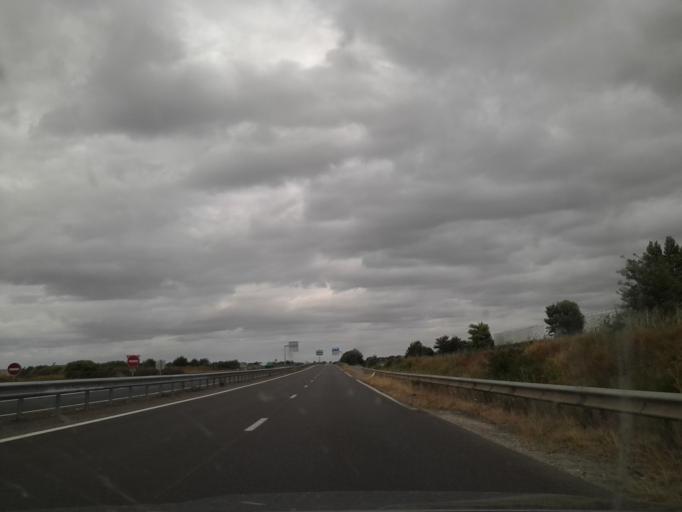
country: FR
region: Centre
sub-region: Departement du Cher
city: La Chapelle-Saint-Ursin
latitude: 47.0464
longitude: 2.3379
